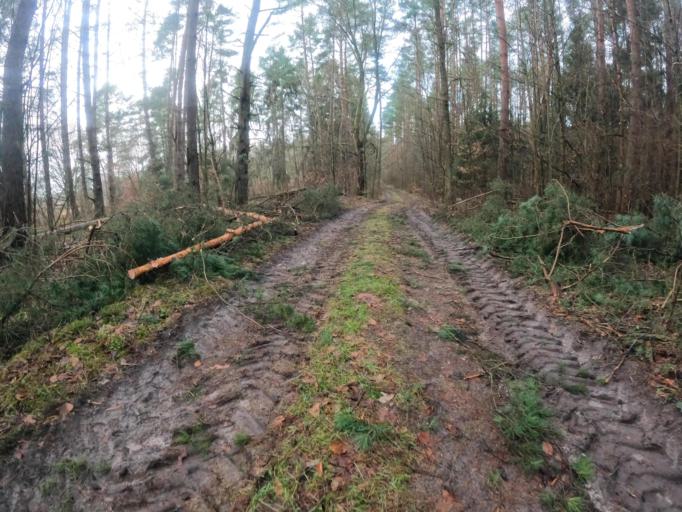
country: PL
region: West Pomeranian Voivodeship
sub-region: Powiat slawienski
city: Slawno
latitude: 54.2446
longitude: 16.6894
